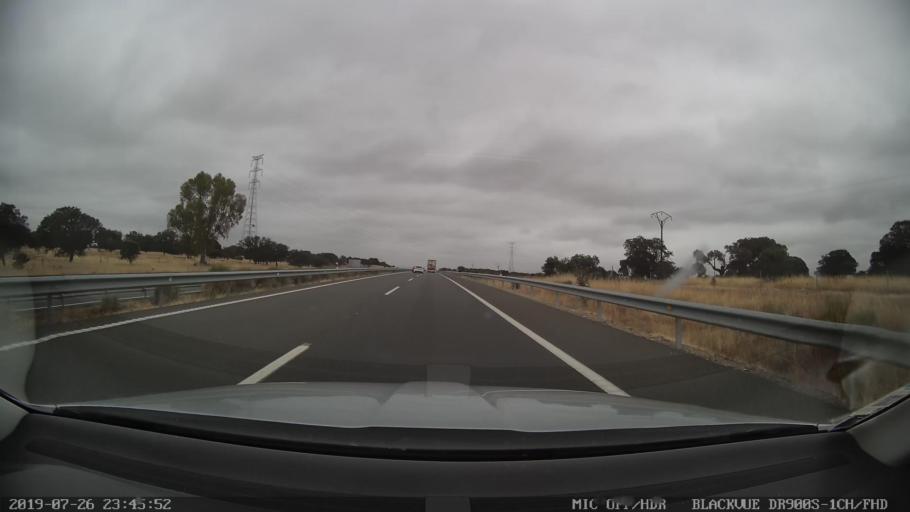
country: ES
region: Extremadura
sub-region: Provincia de Caceres
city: Jaraicejo
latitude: 39.5766
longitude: -5.8343
